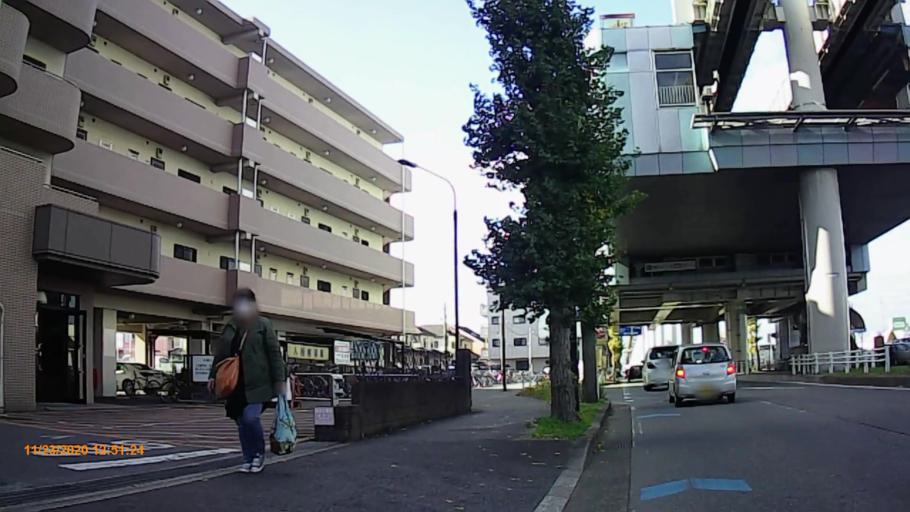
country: JP
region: Chiba
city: Yotsukaido
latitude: 35.6310
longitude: 140.1608
